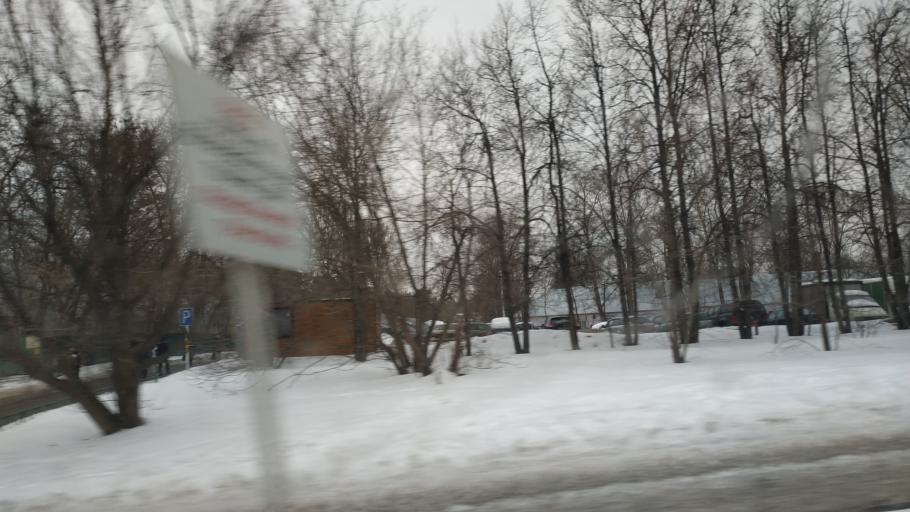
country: RU
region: Moscow
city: Shchukino
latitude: 55.7806
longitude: 37.4409
